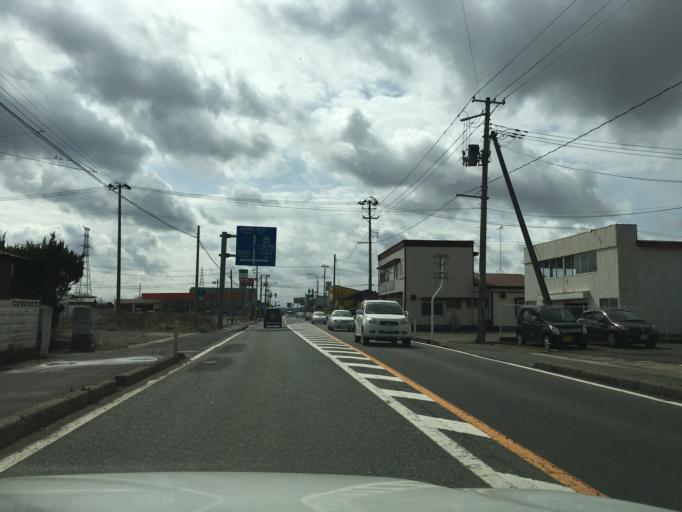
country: JP
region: Akita
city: Tenno
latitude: 39.9457
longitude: 140.0838
